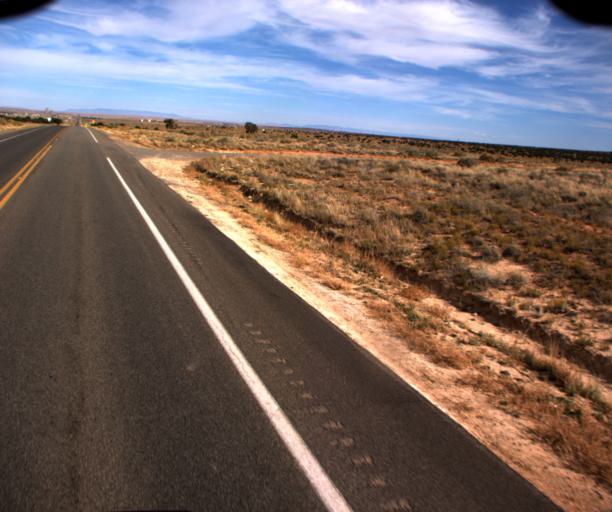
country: US
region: Arizona
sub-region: Navajo County
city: Kayenta
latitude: 36.6999
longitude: -110.2981
